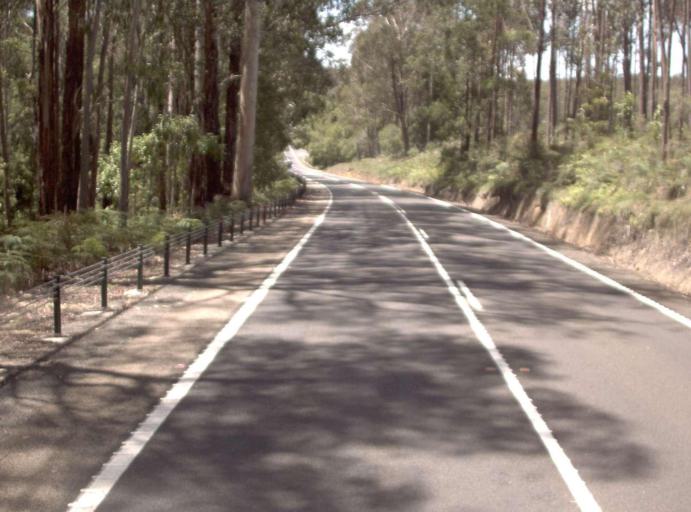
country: AU
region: New South Wales
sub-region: Bombala
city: Bombala
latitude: -37.6549
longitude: 148.8138
